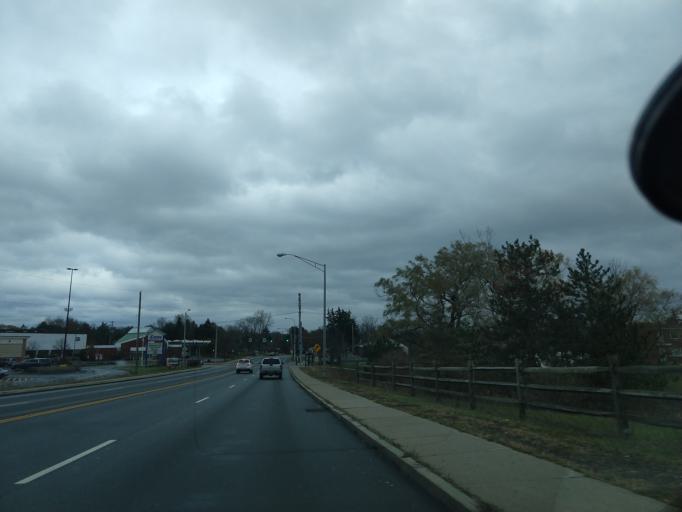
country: US
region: New York
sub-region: Tompkins County
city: Lansing
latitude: 42.4799
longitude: -76.4832
